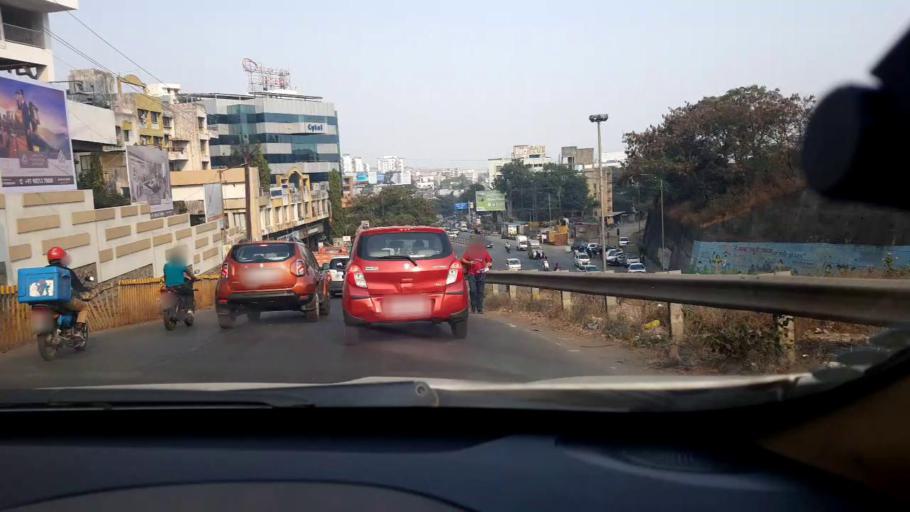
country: IN
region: Maharashtra
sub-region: Pune Division
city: Kharakvasla
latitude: 18.5078
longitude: 73.7874
